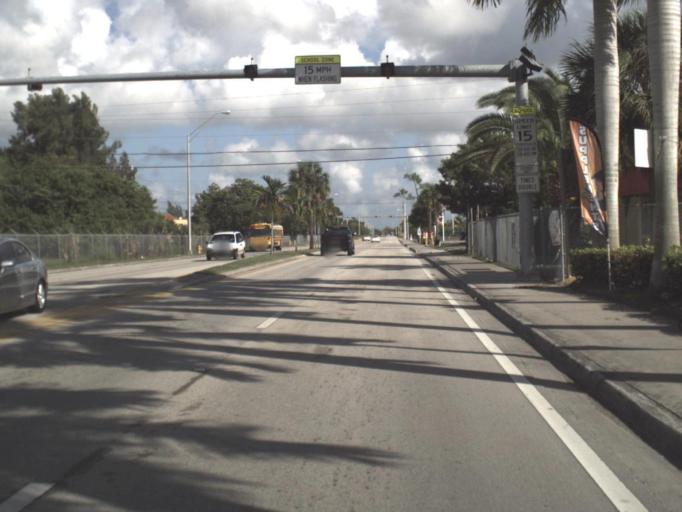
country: US
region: Florida
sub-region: Miami-Dade County
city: Leisure City
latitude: 25.4996
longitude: -80.4069
